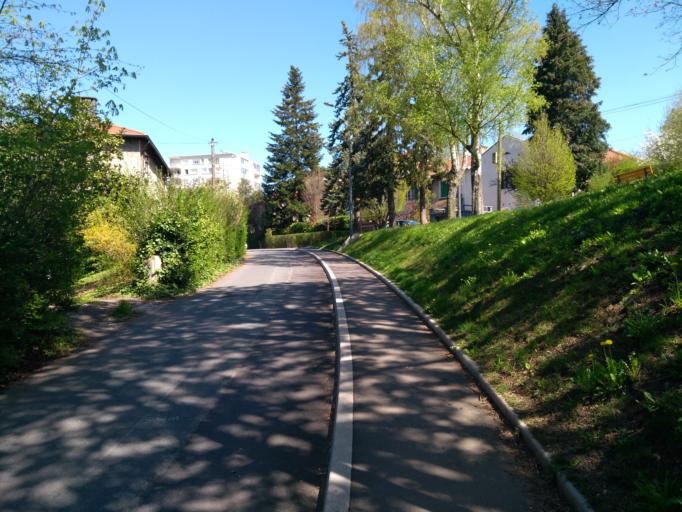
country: FR
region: Rhone-Alpes
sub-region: Departement de la Loire
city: Saint-Etienne
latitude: 45.4277
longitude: 4.4102
